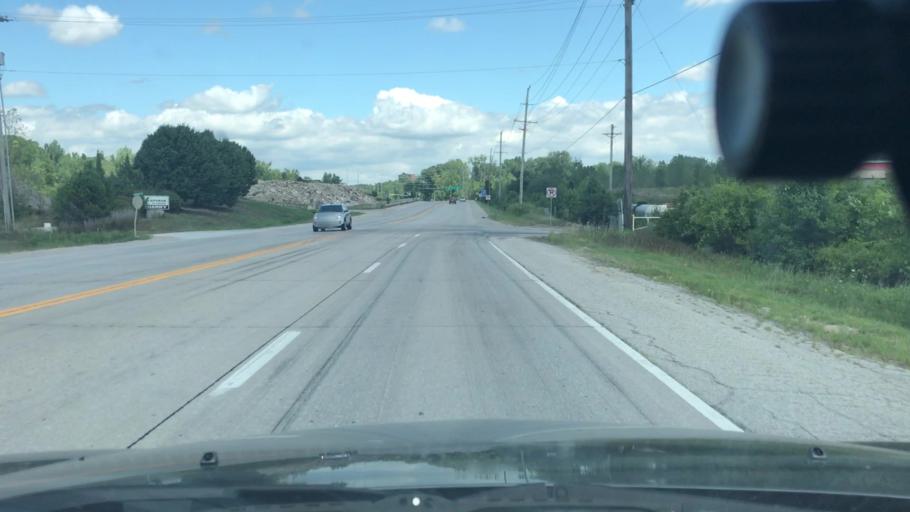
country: US
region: Missouri
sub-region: Saint Charles County
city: Saint Charles
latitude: 38.7512
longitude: -90.5064
